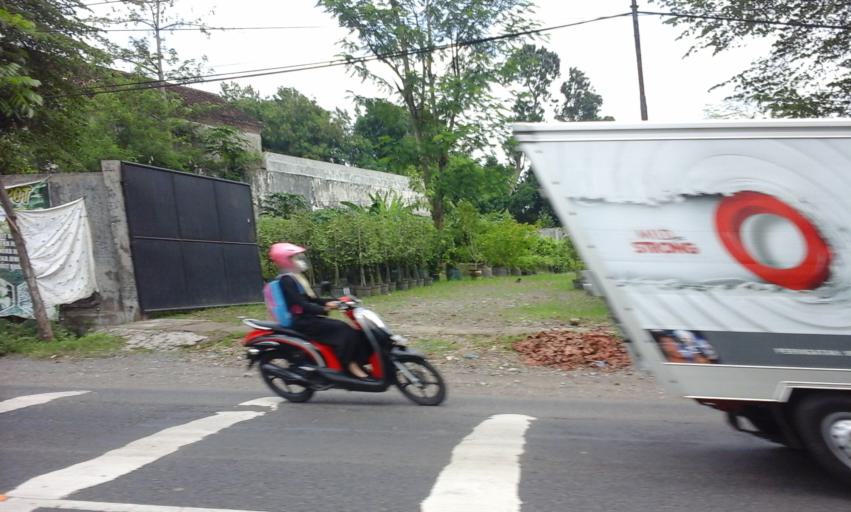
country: ID
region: East Java
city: Jubung
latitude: -8.1944
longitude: 113.6408
